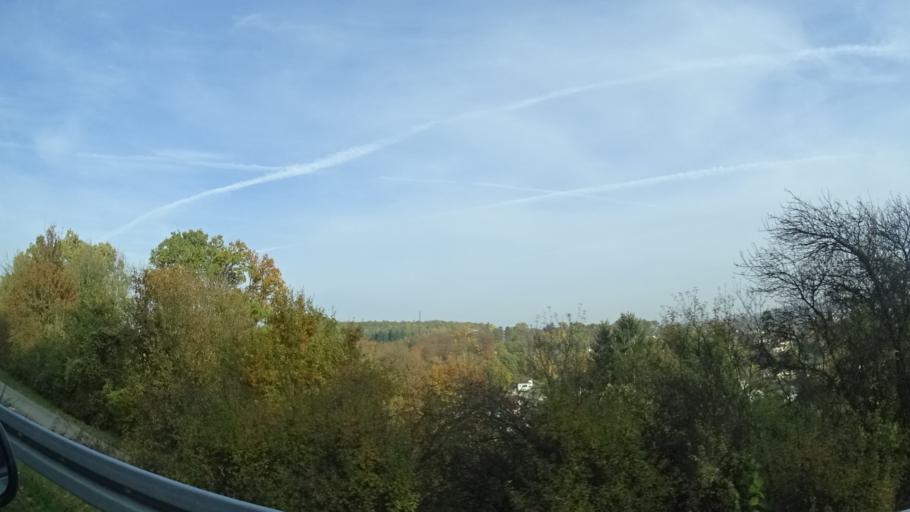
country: DE
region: Baden-Wuerttemberg
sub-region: Karlsruhe Region
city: Adelsheim
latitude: 49.4075
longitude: 9.3827
